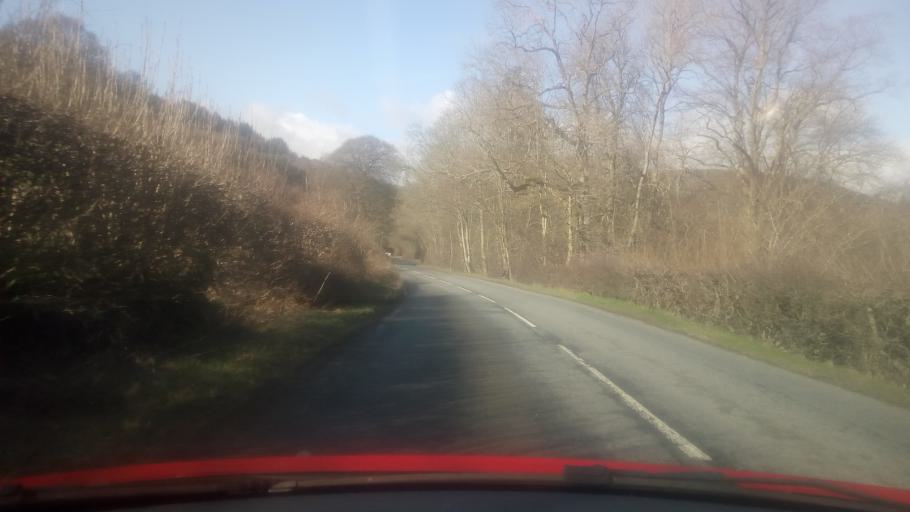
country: GB
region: Scotland
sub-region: The Scottish Borders
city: Selkirk
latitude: 55.5823
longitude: -2.8508
